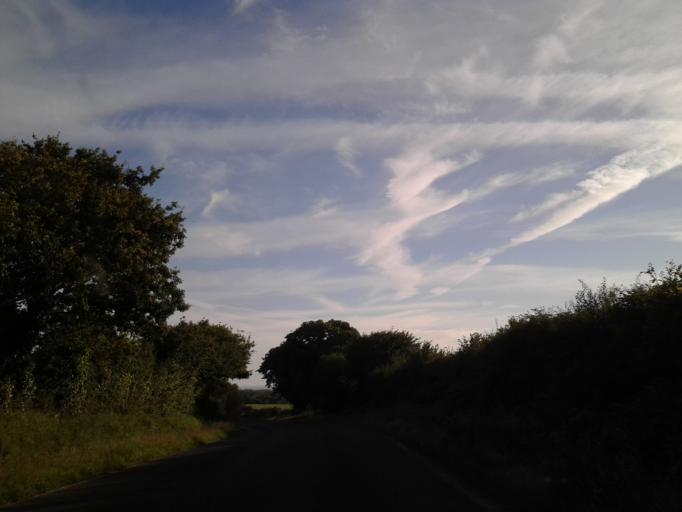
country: FR
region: Lower Normandy
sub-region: Departement de la Manche
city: Fermanville
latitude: 49.6476
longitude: -1.4430
